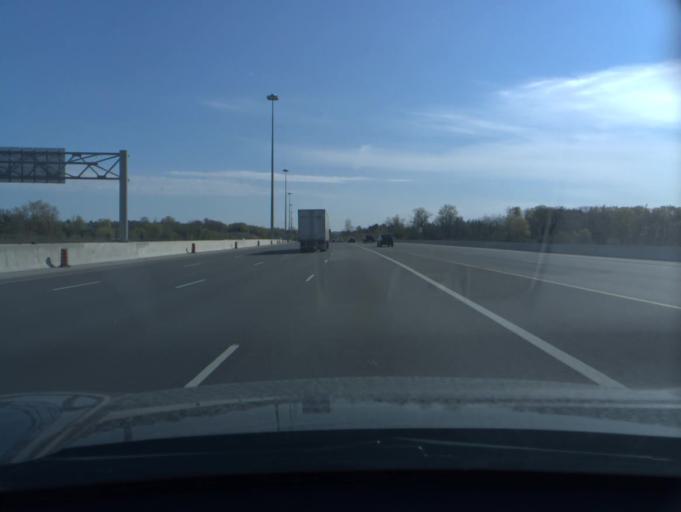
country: CA
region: Ontario
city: North Perth
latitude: 43.8134
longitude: -81.0001
